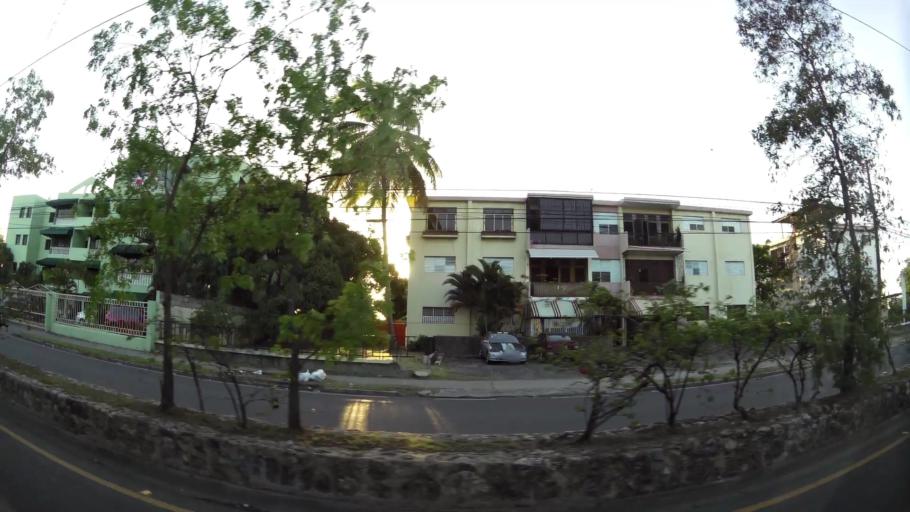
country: DO
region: Nacional
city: La Agustina
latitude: 18.4895
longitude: -69.9597
